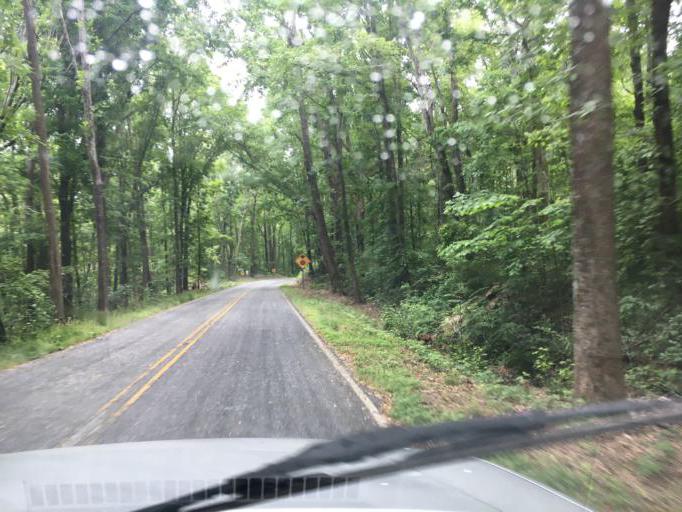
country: US
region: South Carolina
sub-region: Greenville County
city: Tigerville
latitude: 35.1208
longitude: -82.3740
